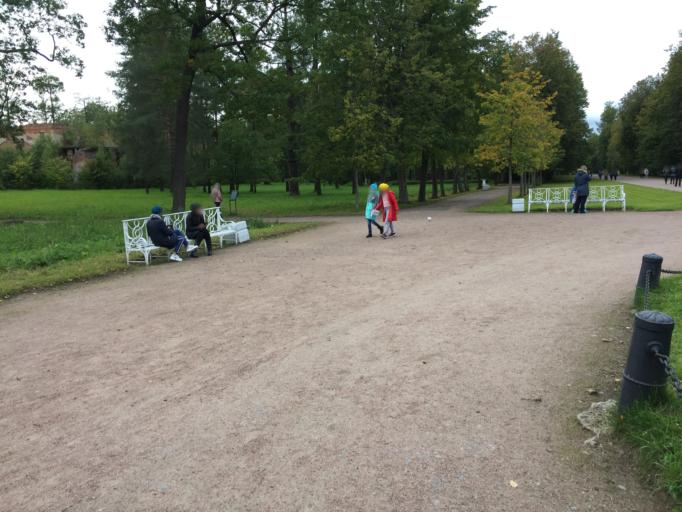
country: RU
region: St.-Petersburg
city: Pushkin
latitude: 59.7180
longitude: 30.3890
